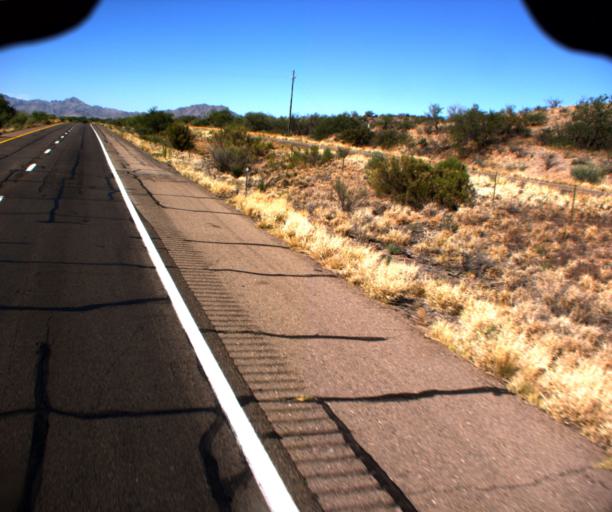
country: US
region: Arizona
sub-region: Pima County
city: Arivaca Junction
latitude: 31.7500
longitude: -111.0443
